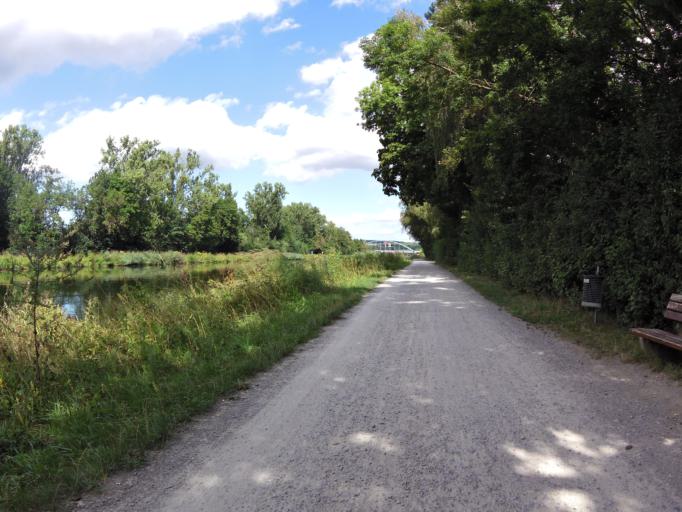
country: DE
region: Bavaria
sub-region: Regierungsbezirk Unterfranken
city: Volkach
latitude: 49.8571
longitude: 10.2243
